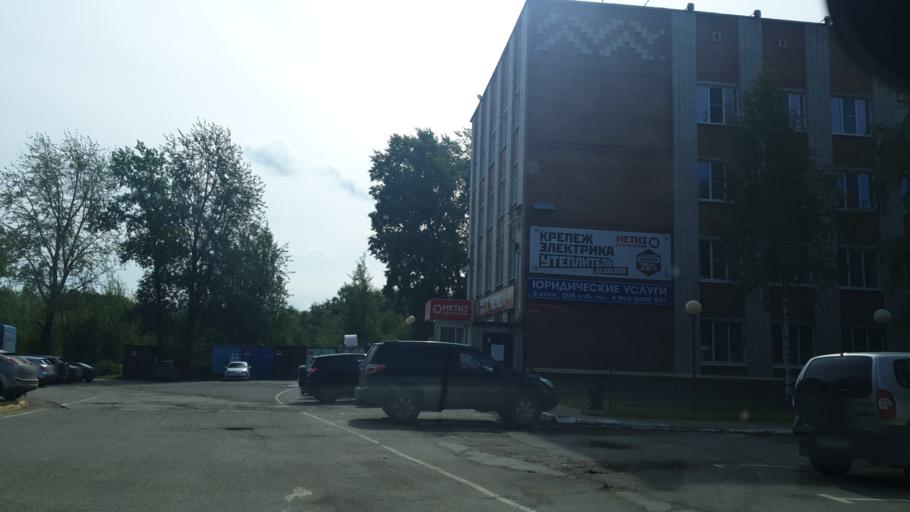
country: RU
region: Komi Republic
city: Ezhva
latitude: 61.8093
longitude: 50.7358
